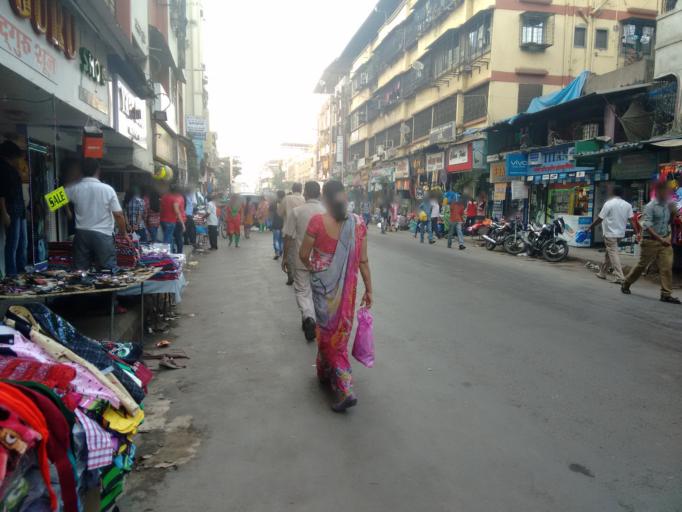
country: IN
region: Maharashtra
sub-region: Thane
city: Bhayandar
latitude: 19.3077
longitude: 72.8552
